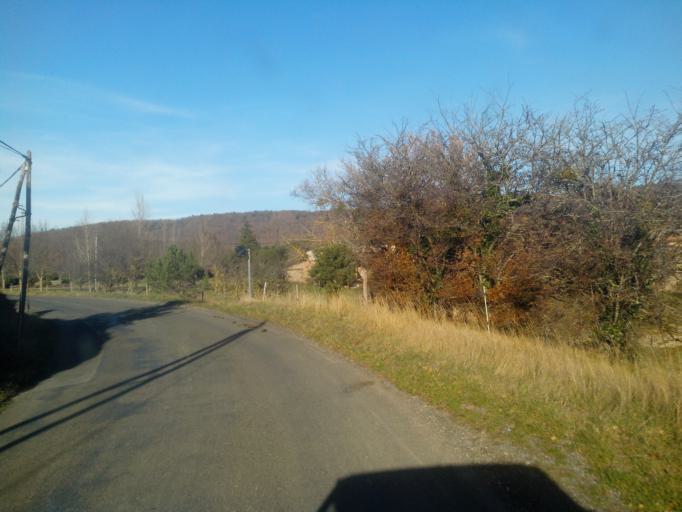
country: FR
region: Languedoc-Roussillon
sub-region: Departement de l'Aude
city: Couiza
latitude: 42.8811
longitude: 2.3221
